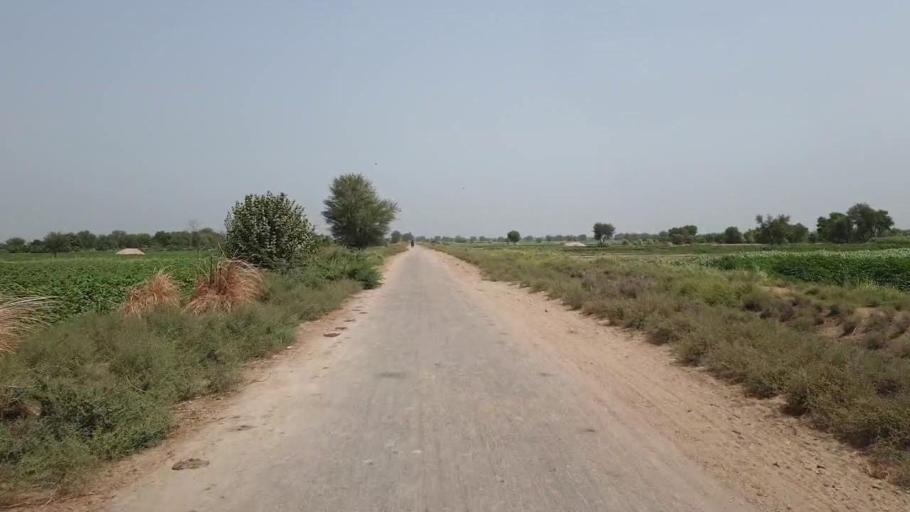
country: PK
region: Sindh
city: Nawabshah
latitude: 26.2697
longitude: 68.3159
